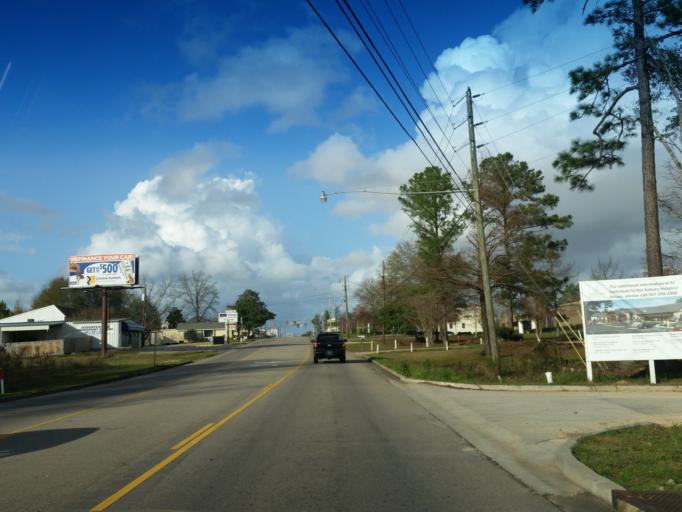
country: US
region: Mississippi
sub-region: Lamar County
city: West Hattiesburg
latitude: 31.3205
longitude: -89.3479
